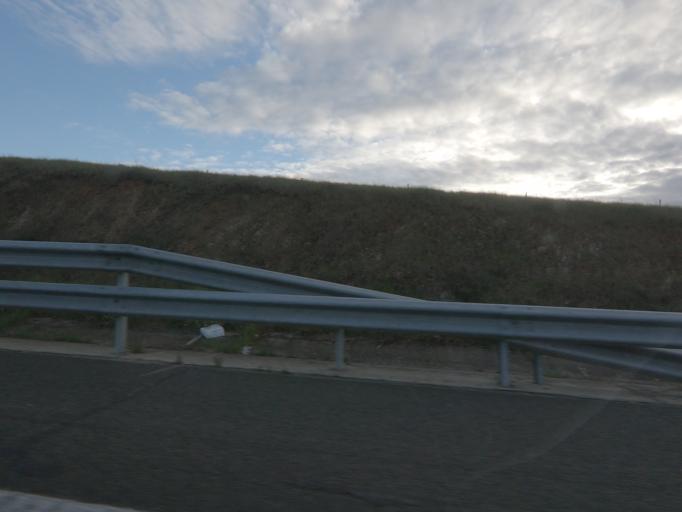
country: ES
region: Extremadura
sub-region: Provincia de Caceres
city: Caceres
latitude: 39.4373
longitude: -6.4105
